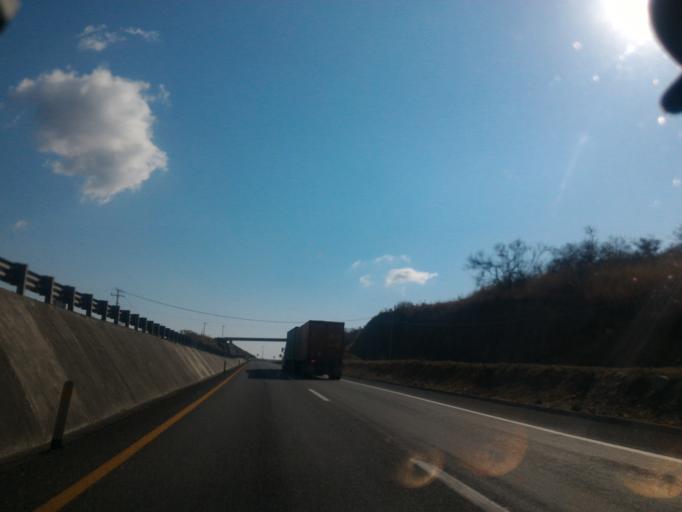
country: MX
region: Jalisco
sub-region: Tonila
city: San Marcos
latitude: 19.4314
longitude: -103.4971
